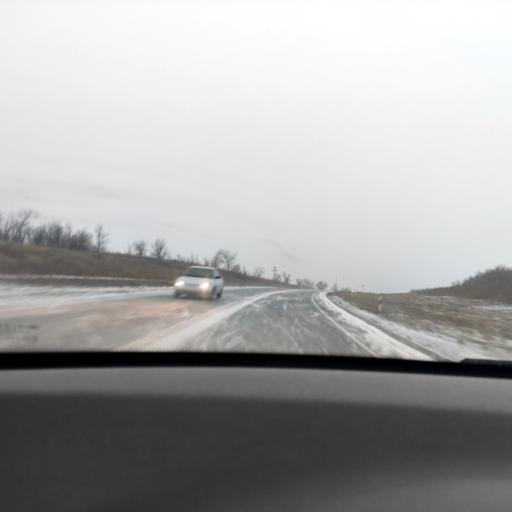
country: RU
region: Samara
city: Novokuybyshevsk
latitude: 52.9082
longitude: 49.9343
